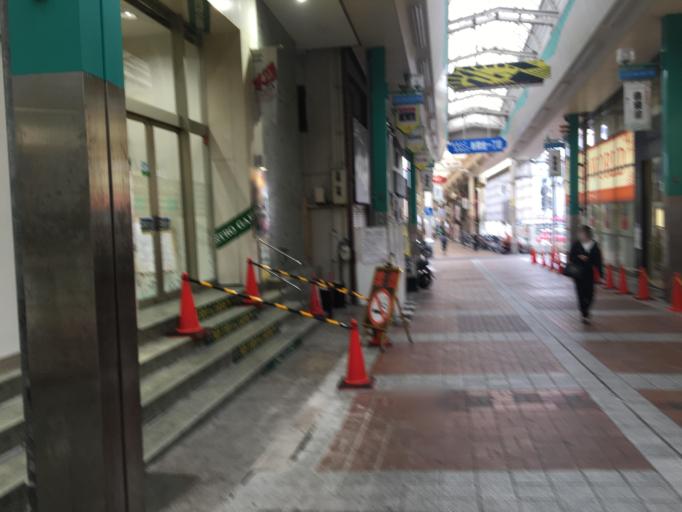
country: JP
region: Hyogo
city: Kobe
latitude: 34.6781
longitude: 135.1689
